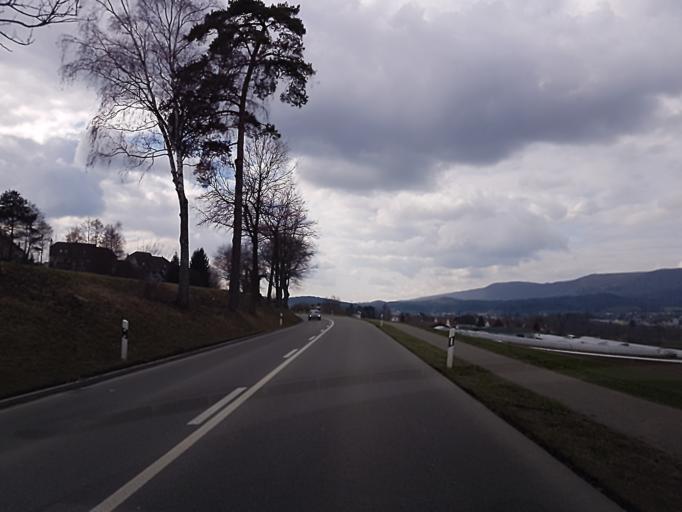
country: CH
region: Zurich
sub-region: Bezirk Dielsdorf
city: Daenikon
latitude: 47.4454
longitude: 8.4139
